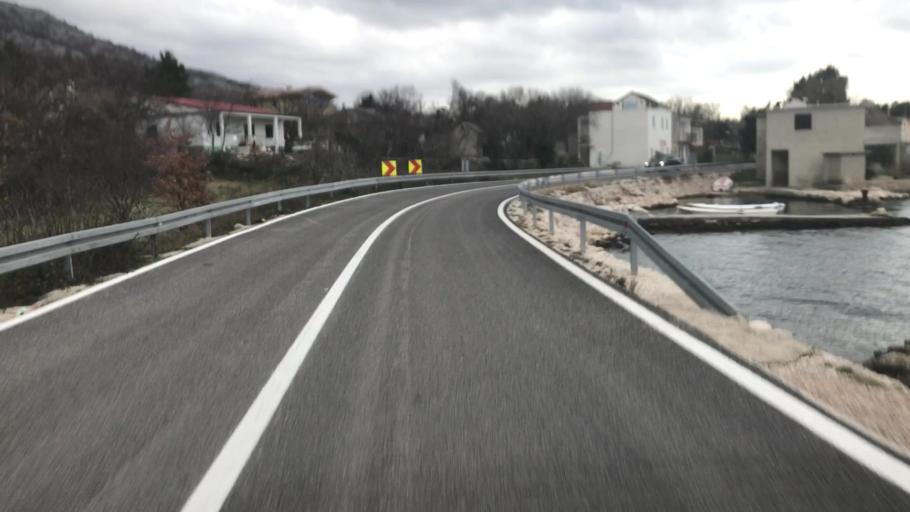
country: HR
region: Zadarska
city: Razanac
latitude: 44.3401
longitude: 15.3381
